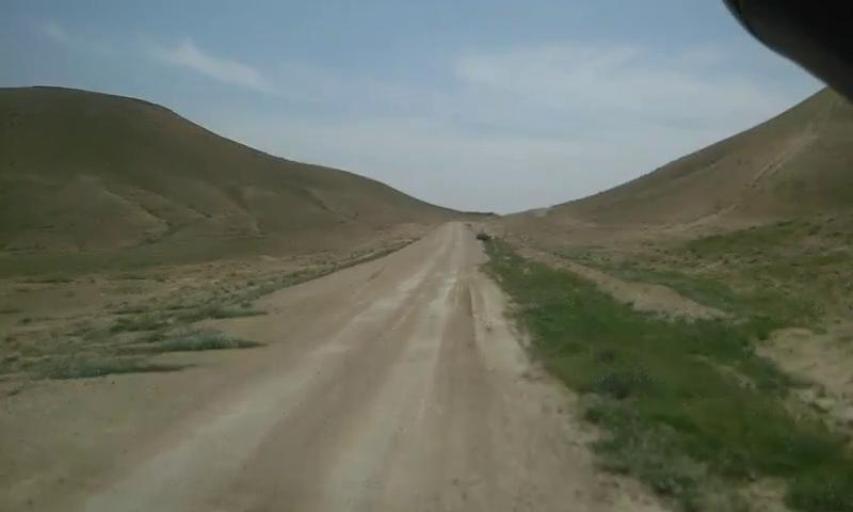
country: PS
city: `Arab ar Rashaydah
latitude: 31.4973
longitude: 35.2939
